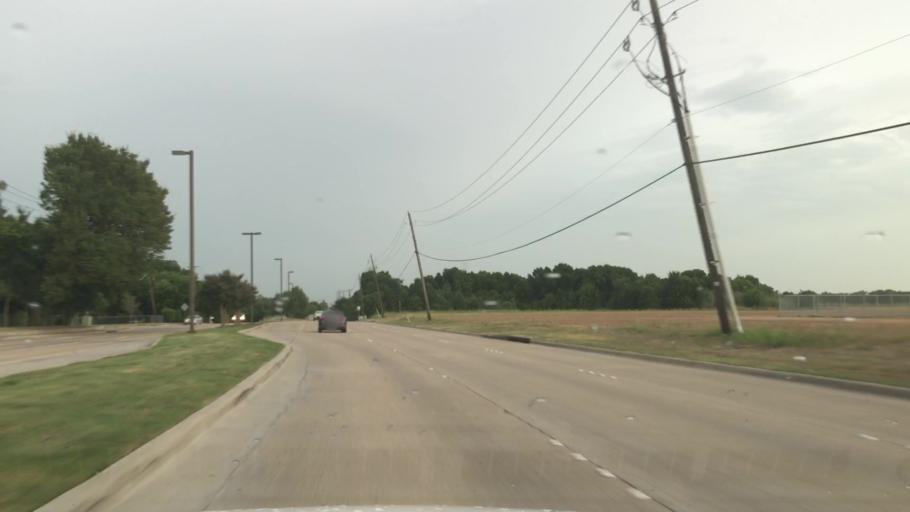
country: US
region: Texas
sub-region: Dallas County
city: Mesquite
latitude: 32.7308
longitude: -96.5544
